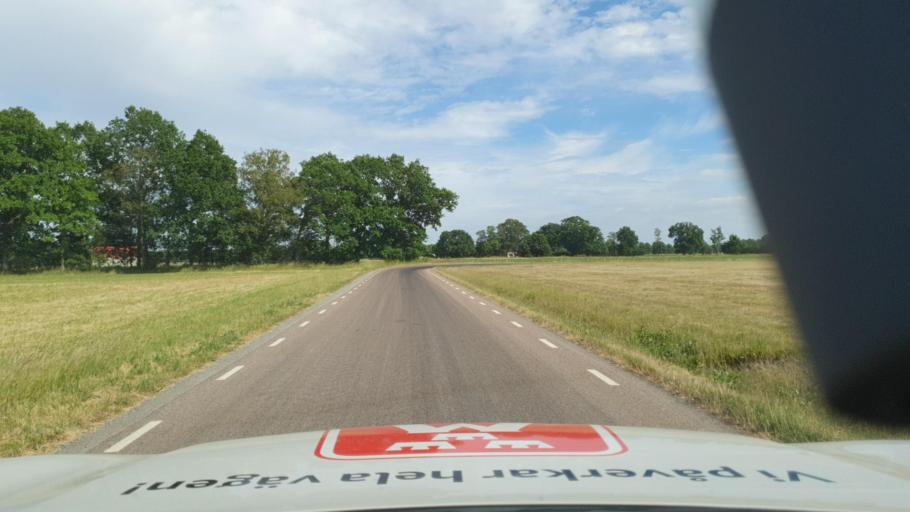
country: SE
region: Skane
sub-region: Sjobo Kommun
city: Blentarp
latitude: 55.6115
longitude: 13.6182
